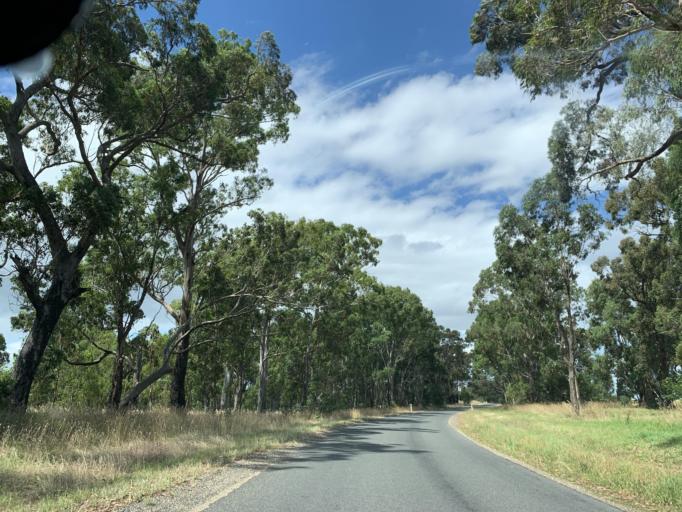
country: AU
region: Victoria
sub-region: Wellington
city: Heyfield
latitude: -37.9075
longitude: 146.7088
